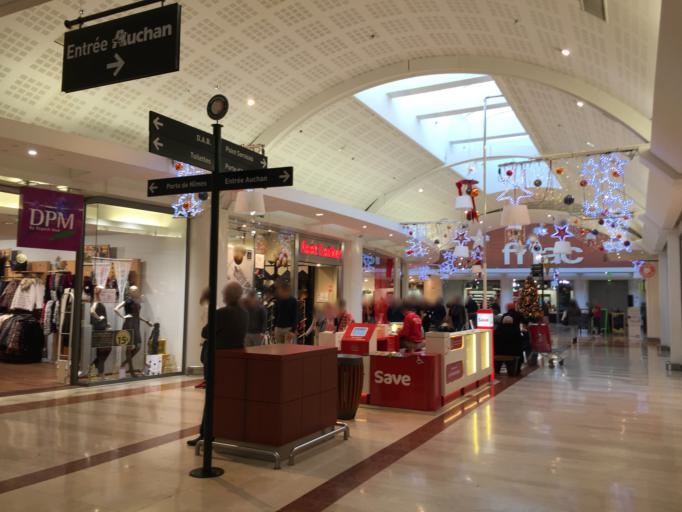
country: FR
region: Provence-Alpes-Cote d'Azur
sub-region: Departement du Vaucluse
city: Vedene
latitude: 43.9816
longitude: 4.8797
